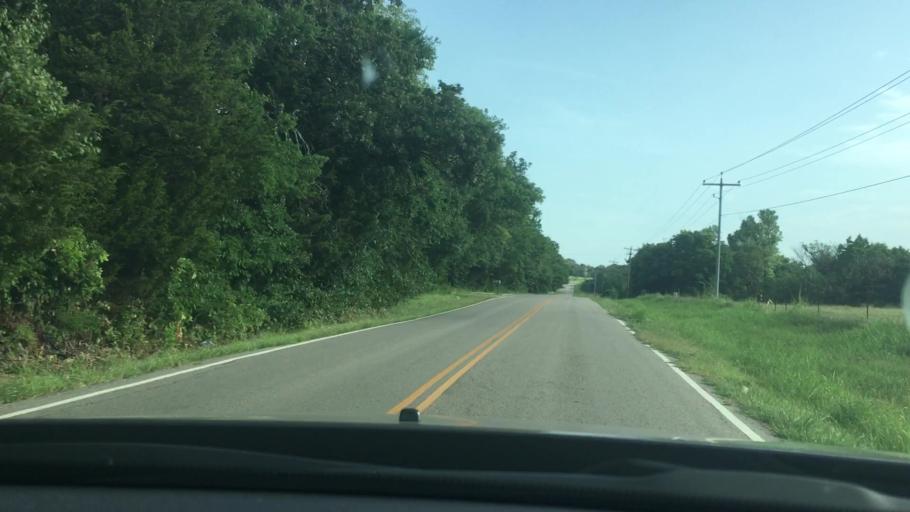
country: US
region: Oklahoma
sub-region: Pontotoc County
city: Byng
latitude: 34.8594
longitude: -96.6135
